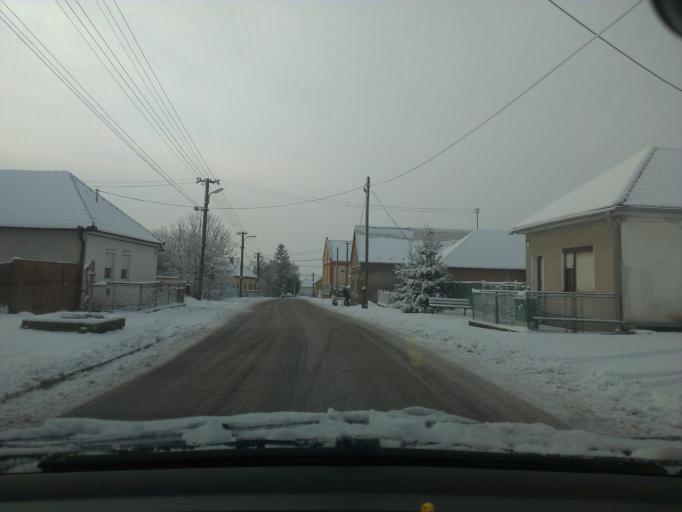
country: SK
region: Trnavsky
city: Hlohovec
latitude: 48.4756
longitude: 17.9882
